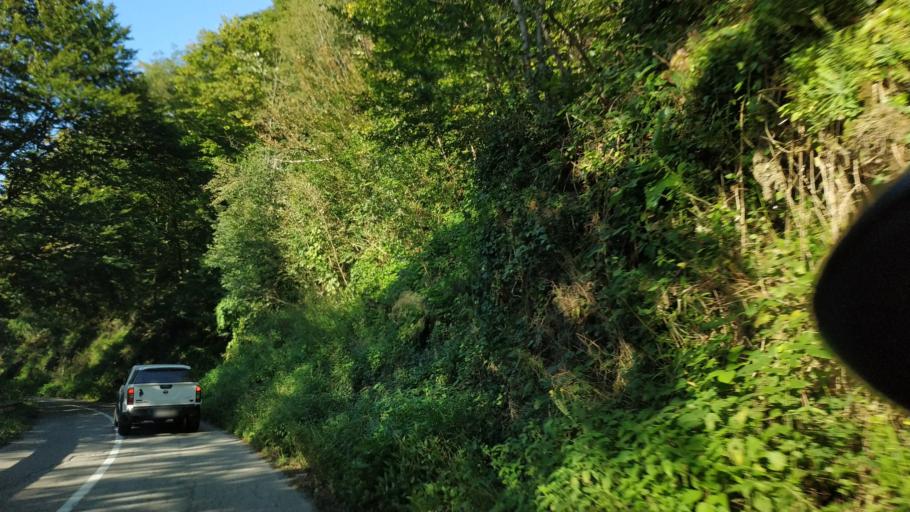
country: RS
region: Central Serbia
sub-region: Rasinski Okrug
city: Krusevac
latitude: 43.4545
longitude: 21.3596
